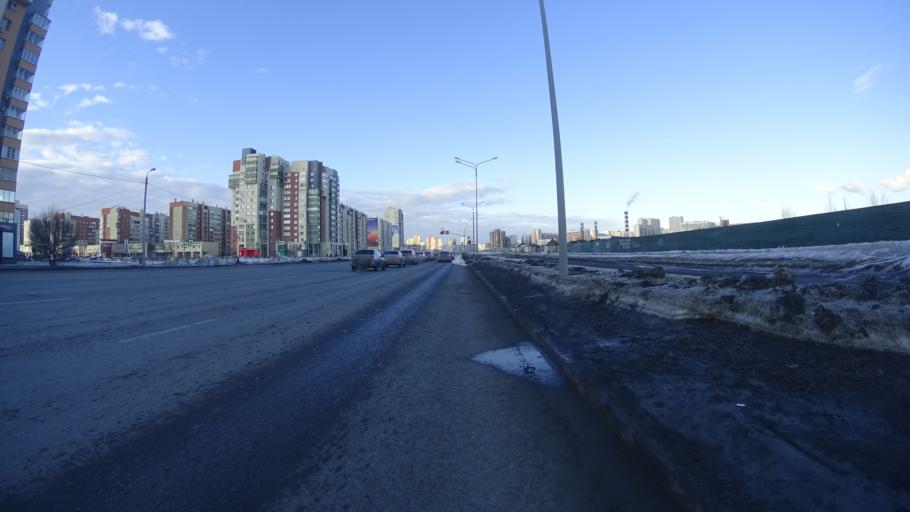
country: RU
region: Chelyabinsk
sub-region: Gorod Chelyabinsk
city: Chelyabinsk
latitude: 55.1622
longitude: 61.3027
